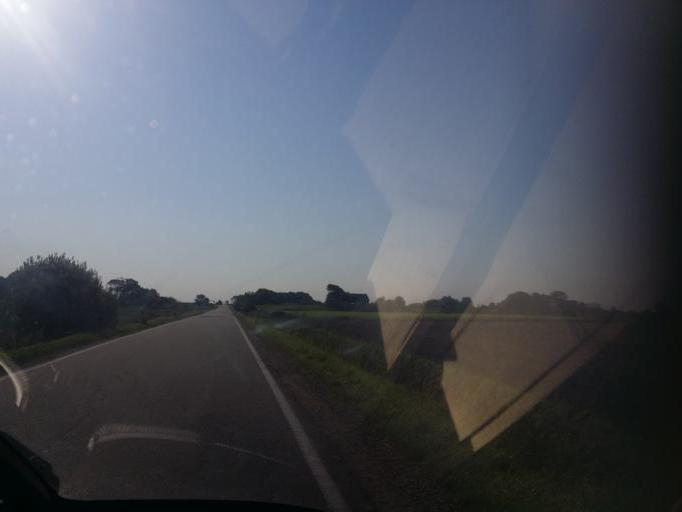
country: DE
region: Schleswig-Holstein
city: Emmelsbull-Horsbull
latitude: 54.8032
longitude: 8.7124
